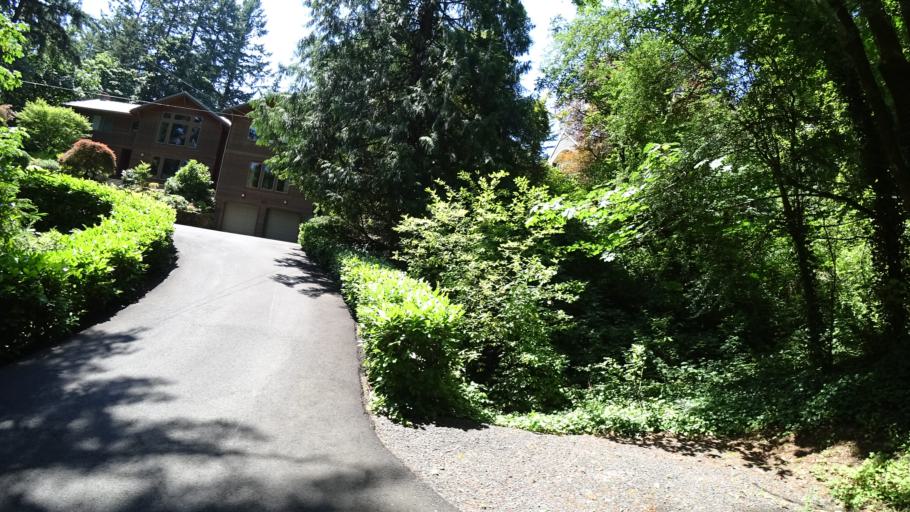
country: US
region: Oregon
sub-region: Multnomah County
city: Portland
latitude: 45.4926
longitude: -122.6852
